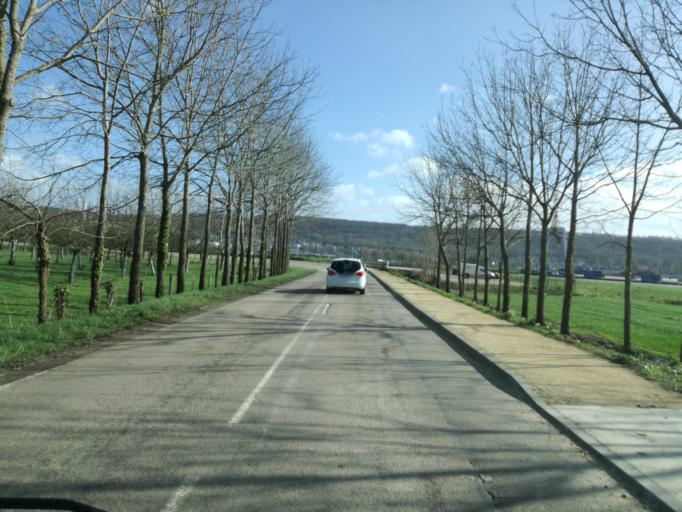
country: FR
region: Haute-Normandie
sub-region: Departement de la Seine-Maritime
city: Grand-Couronne
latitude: 49.3581
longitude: 0.9810
